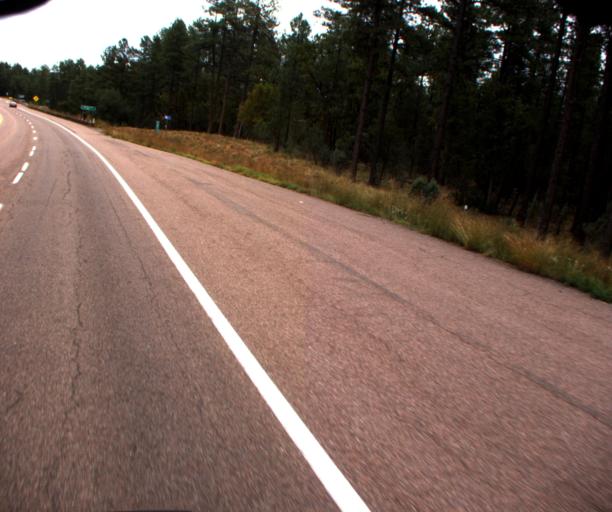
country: US
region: Arizona
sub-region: Gila County
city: Star Valley
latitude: 34.2939
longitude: -110.9768
